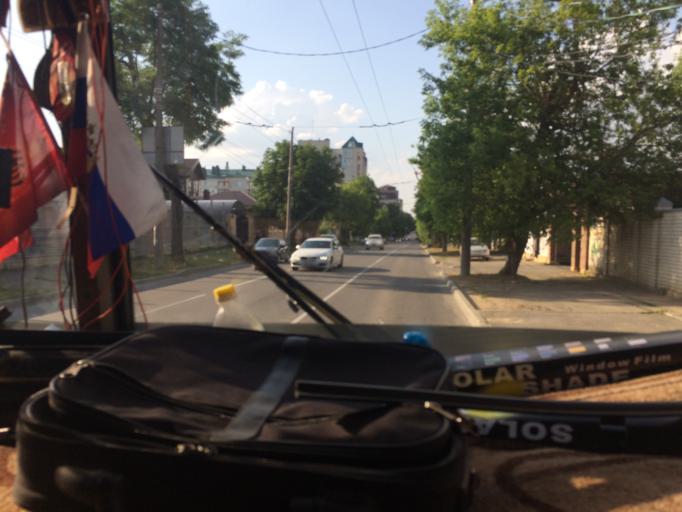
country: RU
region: Stavropol'skiy
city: Stavropol'
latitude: 45.0290
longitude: 41.9533
